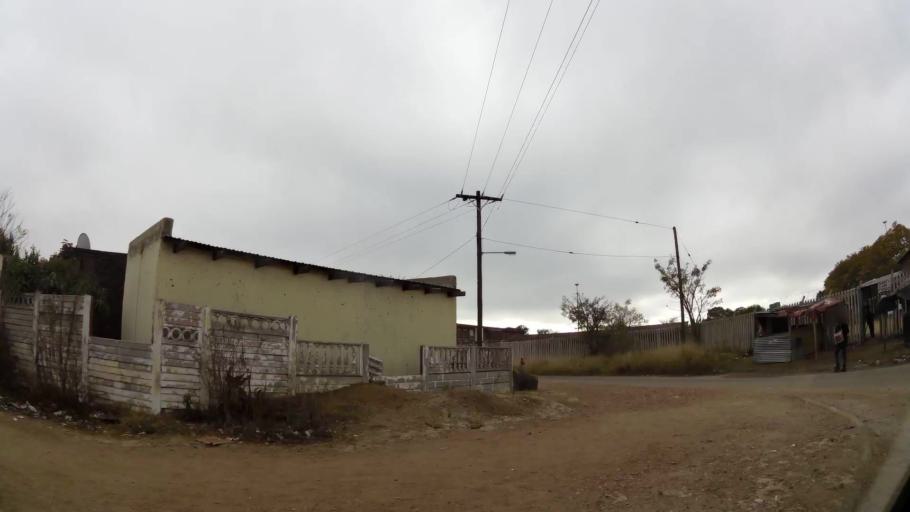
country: ZA
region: Limpopo
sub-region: Capricorn District Municipality
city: Polokwane
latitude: -23.8403
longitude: 29.3914
